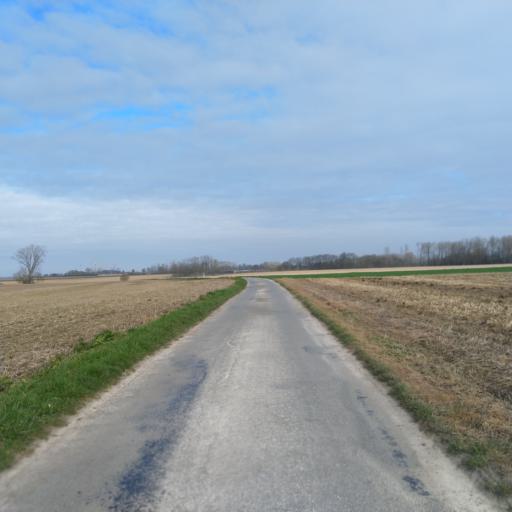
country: BE
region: Wallonia
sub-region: Province du Hainaut
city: Lens
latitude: 50.5725
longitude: 3.8984
